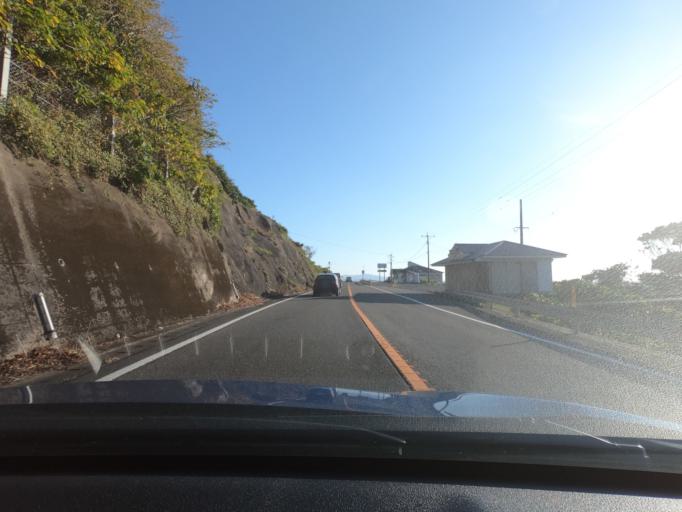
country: JP
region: Kagoshima
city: Akune
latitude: 31.9590
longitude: 130.2143
